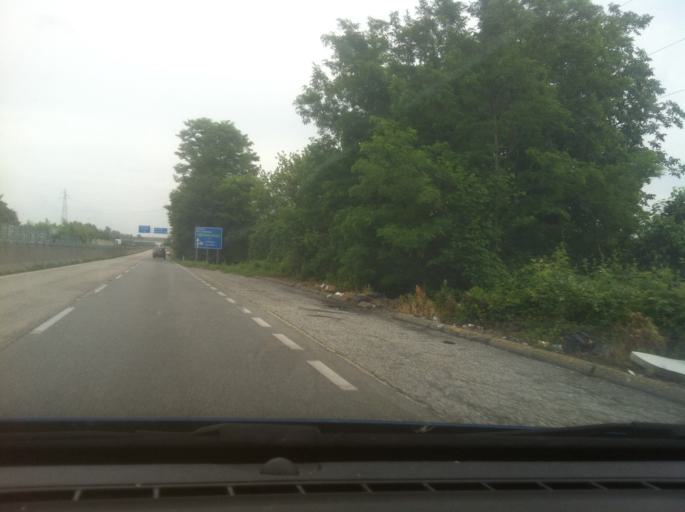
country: IT
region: Piedmont
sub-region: Provincia di Torino
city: San Mauro Torinese
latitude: 45.1153
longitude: 7.7554
